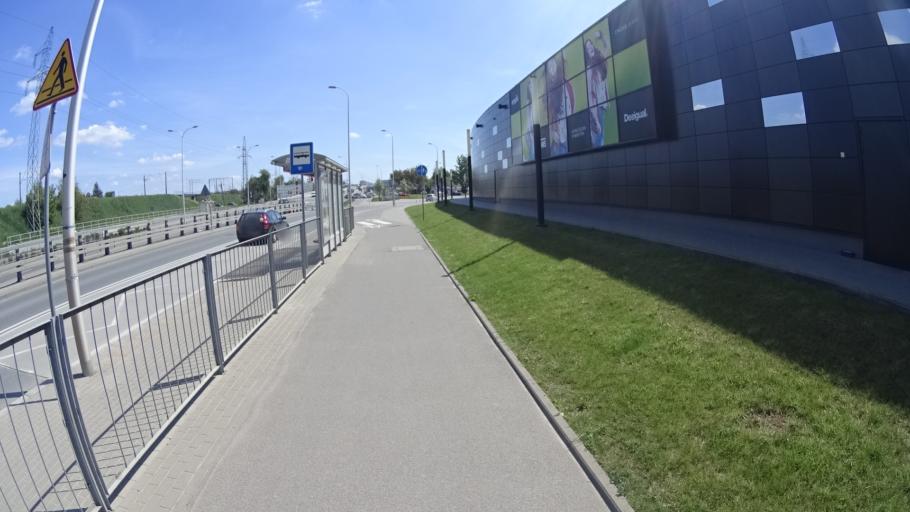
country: PL
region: Masovian Voivodeship
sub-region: Warszawa
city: Ursus
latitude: 52.2032
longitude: 20.8939
